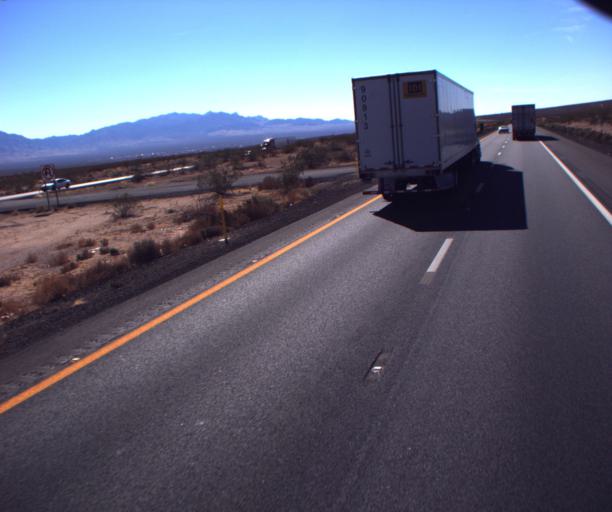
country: US
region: Arizona
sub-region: Mohave County
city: Beaver Dam
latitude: 36.8688
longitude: -113.9660
